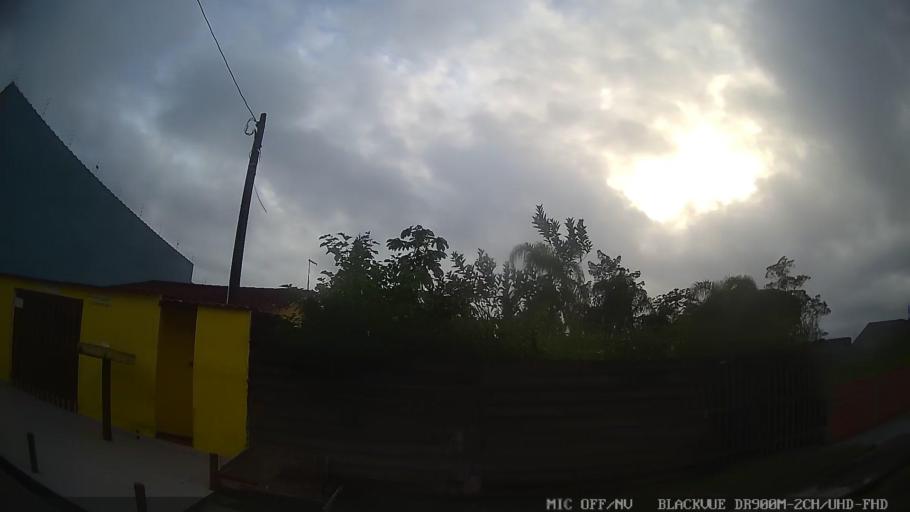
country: BR
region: Sao Paulo
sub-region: Itanhaem
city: Itanhaem
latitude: -24.2312
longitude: -46.8834
